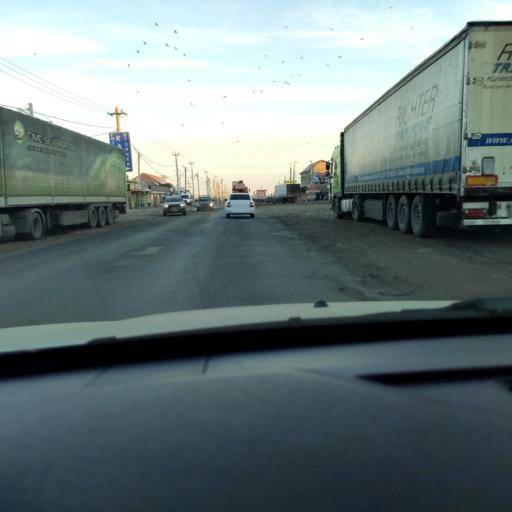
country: RU
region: Samara
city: Smyshlyayevka
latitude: 53.2502
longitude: 50.4747
